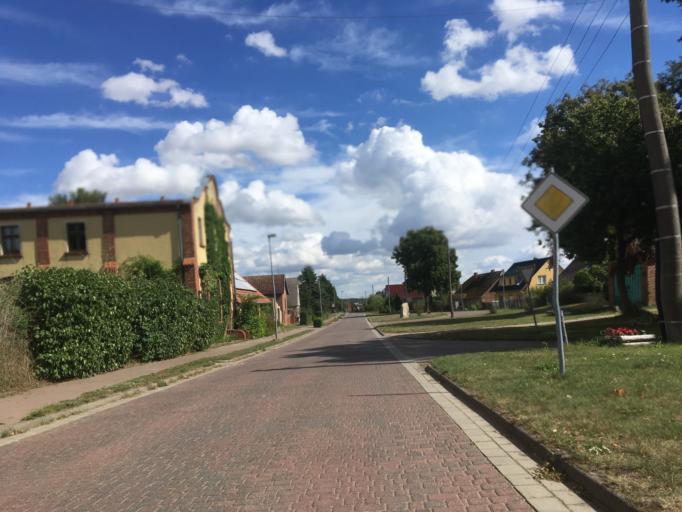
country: DE
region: Brandenburg
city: Angermunde
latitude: 53.0945
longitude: 13.8787
